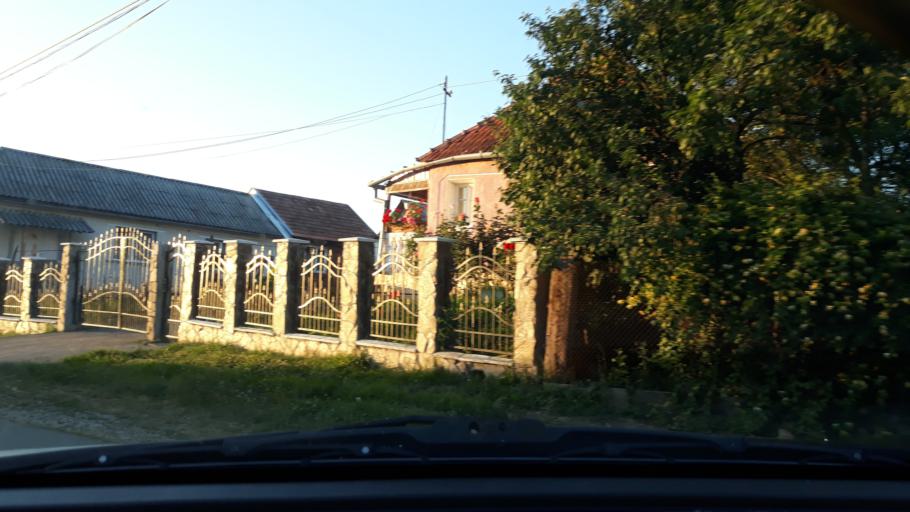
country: RO
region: Bihor
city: Hidiselu de Sus
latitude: 46.9389
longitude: 22.0225
